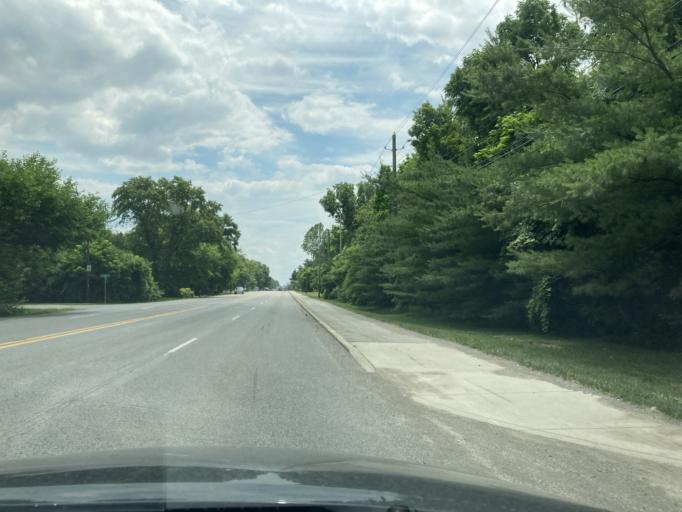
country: US
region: Indiana
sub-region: Marion County
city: Meridian Hills
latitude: 39.8758
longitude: -86.2055
